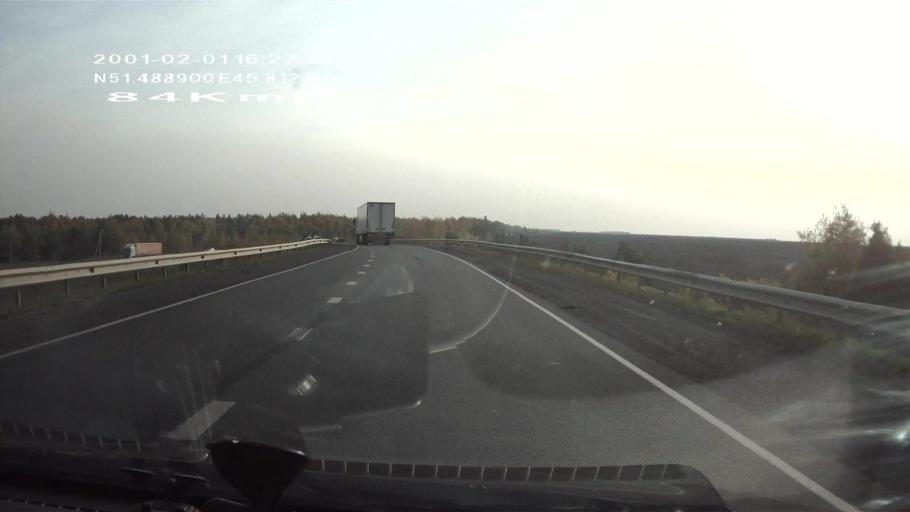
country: RU
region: Saratov
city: Sokolovyy
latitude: 51.4882
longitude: 45.8110
